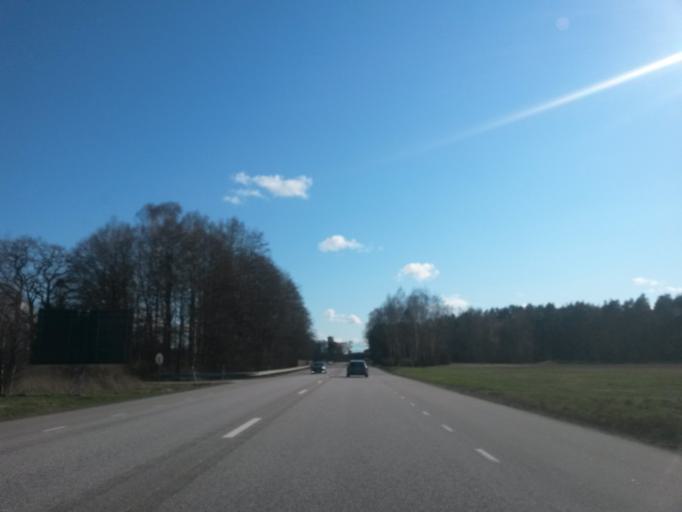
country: SE
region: Vaestra Goetaland
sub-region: Vara Kommun
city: Vara
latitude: 58.2305
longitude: 12.9261
